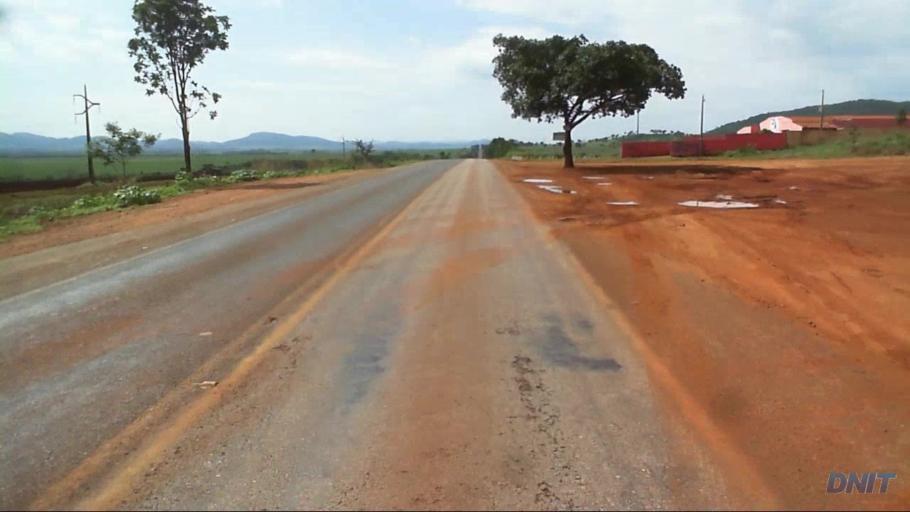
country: BR
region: Goias
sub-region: Barro Alto
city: Barro Alto
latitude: -14.9997
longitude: -48.9052
